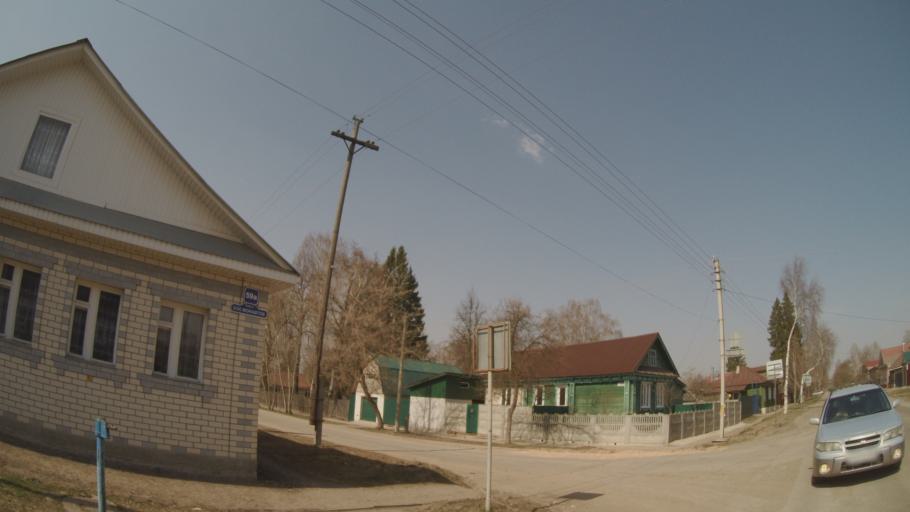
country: RU
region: Nizjnij Novgorod
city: Arzamas
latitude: 55.3888
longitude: 43.8247
